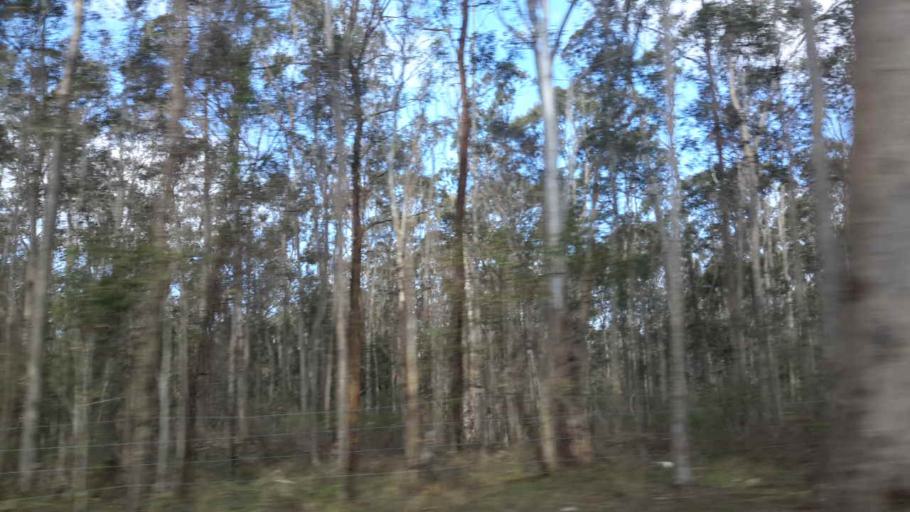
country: AU
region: New South Wales
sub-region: Campbelltown Municipality
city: Glen Alpine
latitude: -34.1433
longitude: 150.7906
